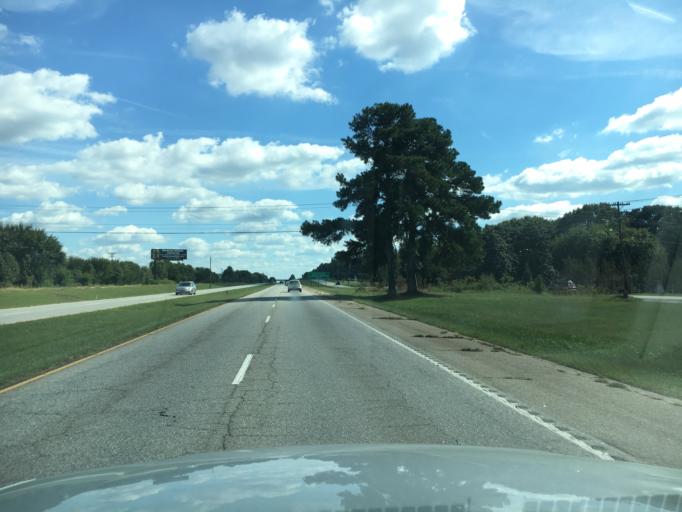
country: US
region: South Carolina
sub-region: Greenville County
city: Mauldin
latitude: 34.7679
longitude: -82.2984
